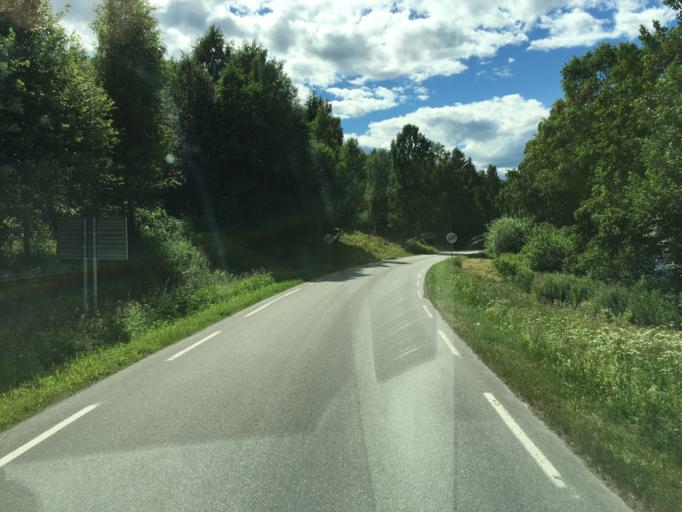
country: NO
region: Oppland
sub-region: Sondre Land
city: Hov
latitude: 60.5116
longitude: 10.3346
